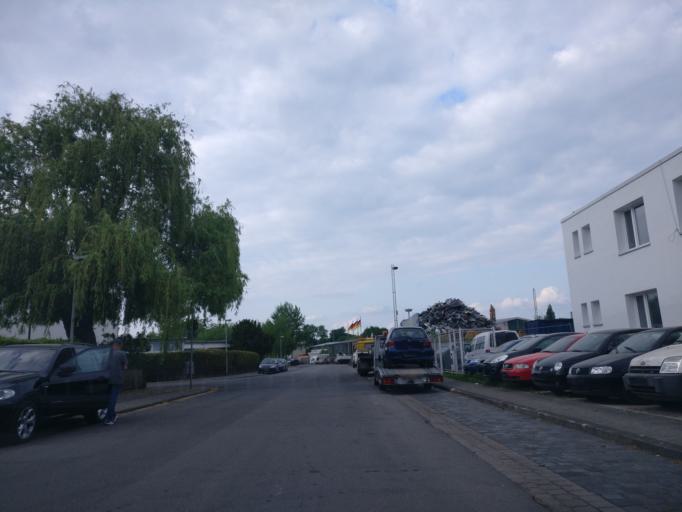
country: DE
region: Lower Saxony
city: Laatzen
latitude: 52.3313
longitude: 9.7820
